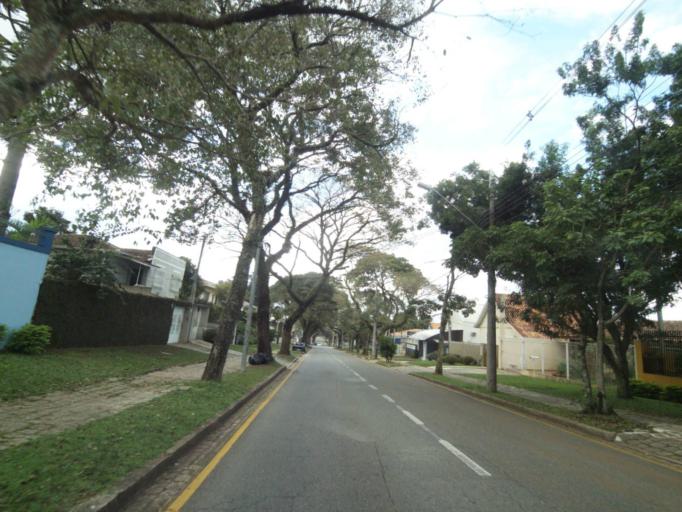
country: BR
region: Parana
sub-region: Curitiba
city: Curitiba
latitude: -25.4165
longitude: -49.2766
